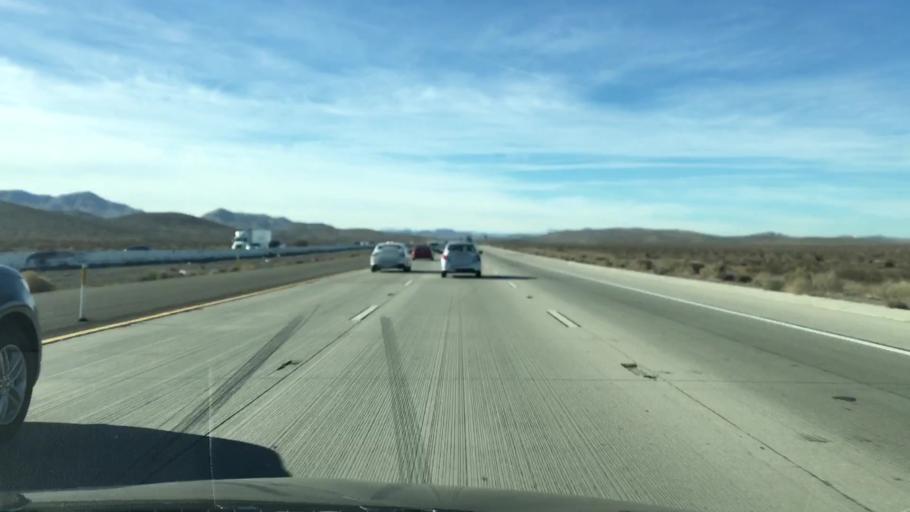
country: US
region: California
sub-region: San Bernardino County
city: Lenwood
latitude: 34.7742
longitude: -117.1408
